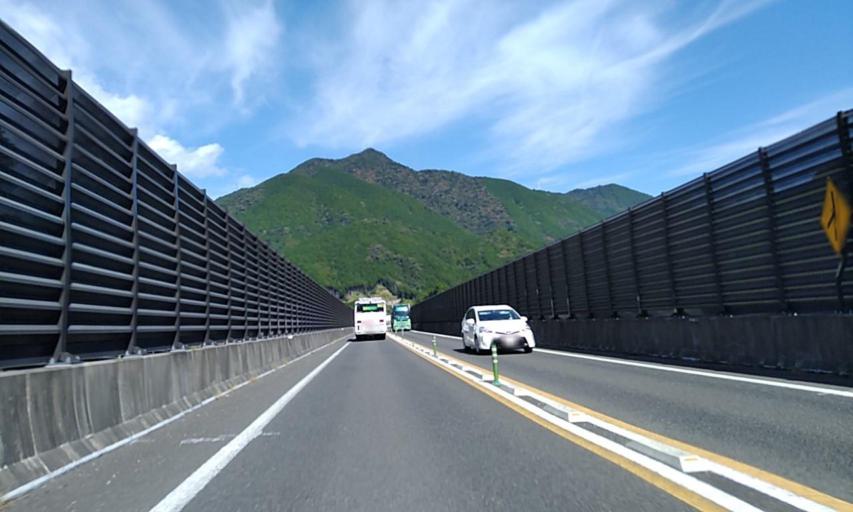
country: JP
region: Mie
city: Owase
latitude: 33.9686
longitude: 136.1620
